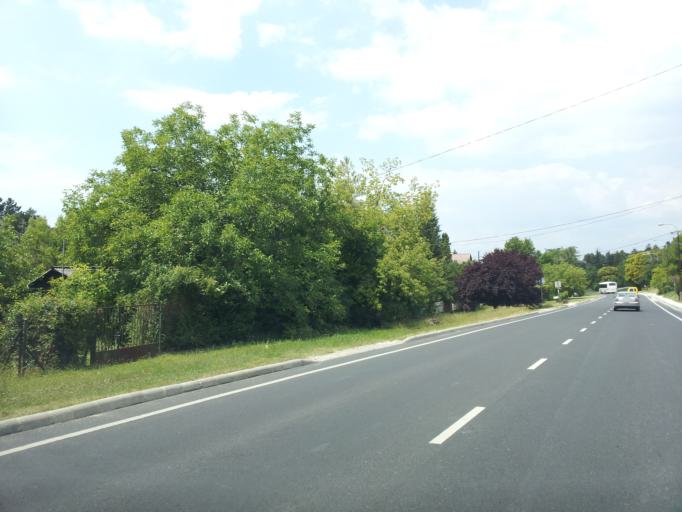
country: HU
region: Veszprem
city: Balatonkenese
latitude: 47.0221
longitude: 18.1487
